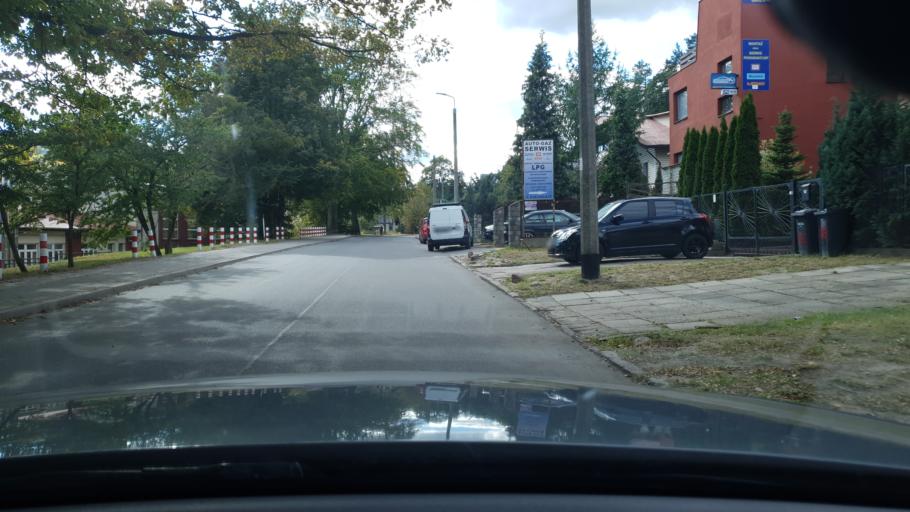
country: PL
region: Pomeranian Voivodeship
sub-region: Powiat wejherowski
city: Reda
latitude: 54.5968
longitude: 18.3443
